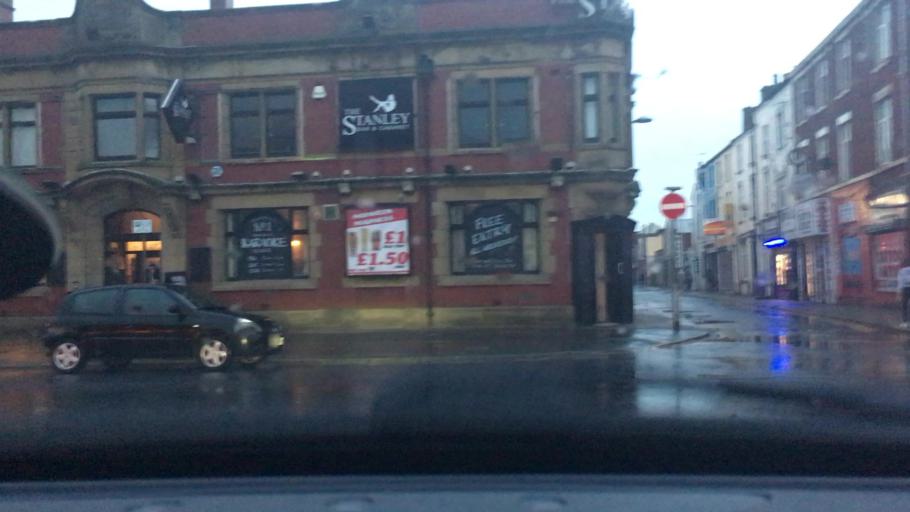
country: GB
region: England
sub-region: Blackpool
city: Blackpool
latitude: 53.8113
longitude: -3.0543
